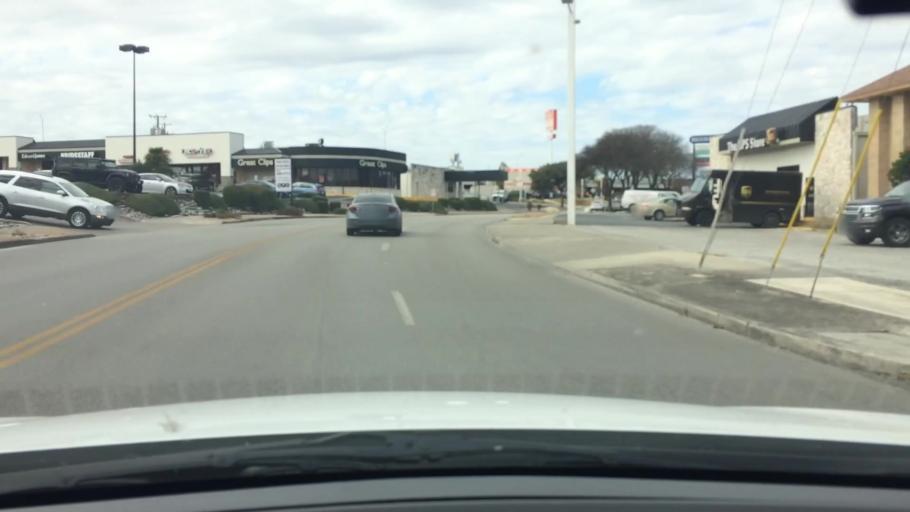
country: US
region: Texas
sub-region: Bexar County
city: Hollywood Park
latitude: 29.5789
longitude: -98.4747
